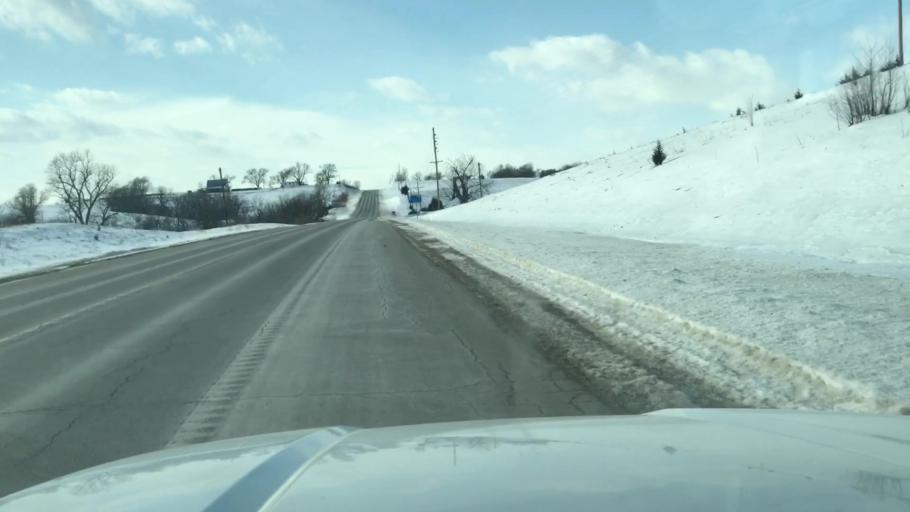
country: US
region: Missouri
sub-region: Nodaway County
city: Maryville
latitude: 40.3436
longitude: -94.6965
